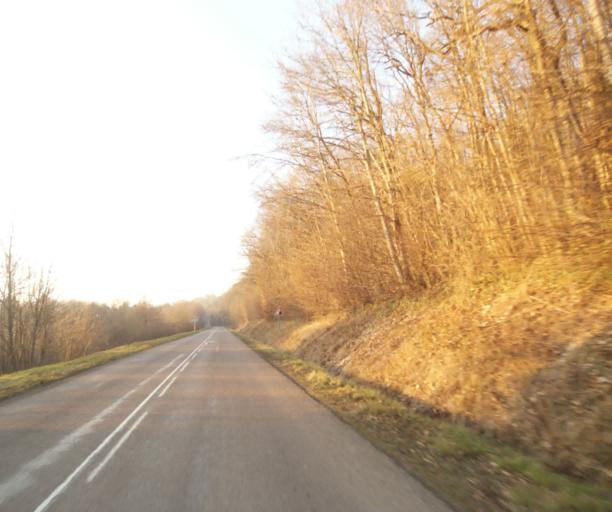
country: FR
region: Lorraine
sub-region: Departement de la Meuse
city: Ancerville
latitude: 48.6119
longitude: 5.0458
